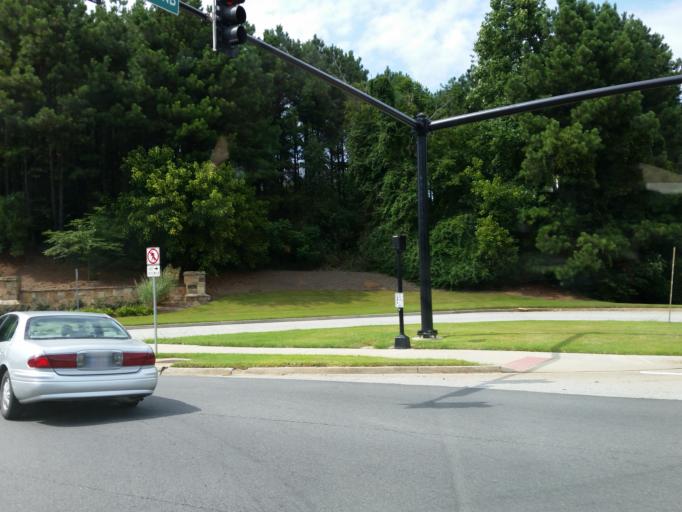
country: US
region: Georgia
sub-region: Fulton County
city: Alpharetta
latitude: 34.0385
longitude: -84.3092
